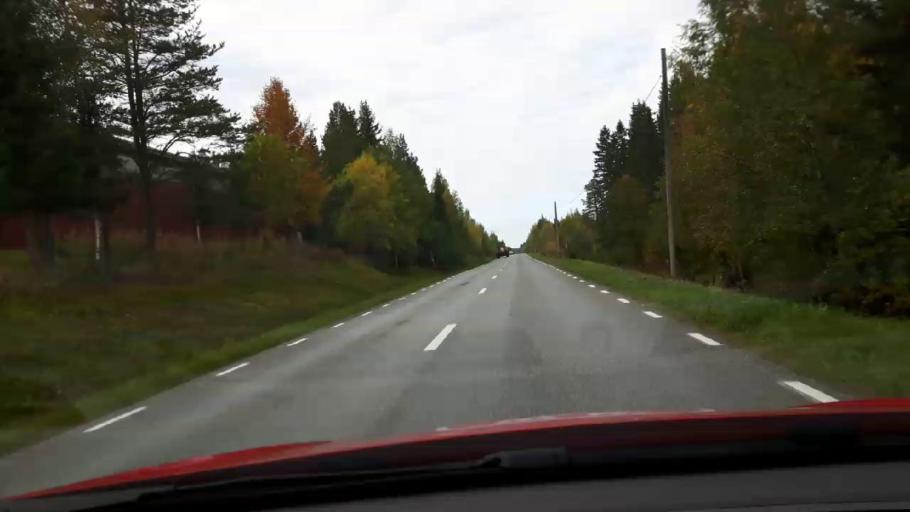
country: SE
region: Jaemtland
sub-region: Krokoms Kommun
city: Krokom
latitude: 63.1886
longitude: 14.0644
